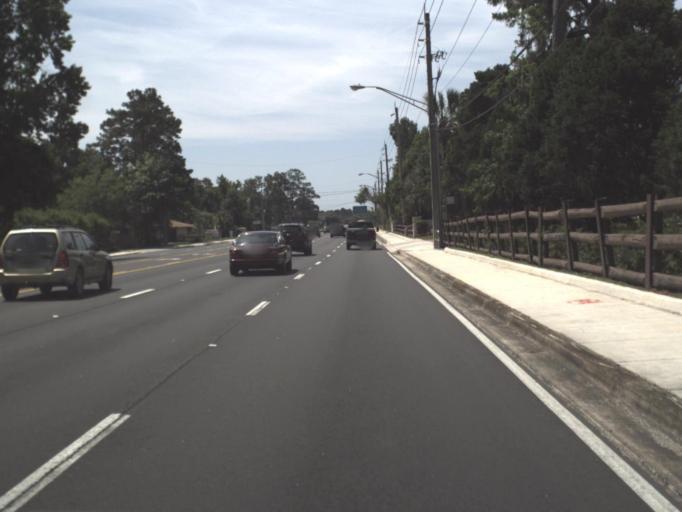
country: US
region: Florida
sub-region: Clay County
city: Orange Park
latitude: 30.2105
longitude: -81.6175
